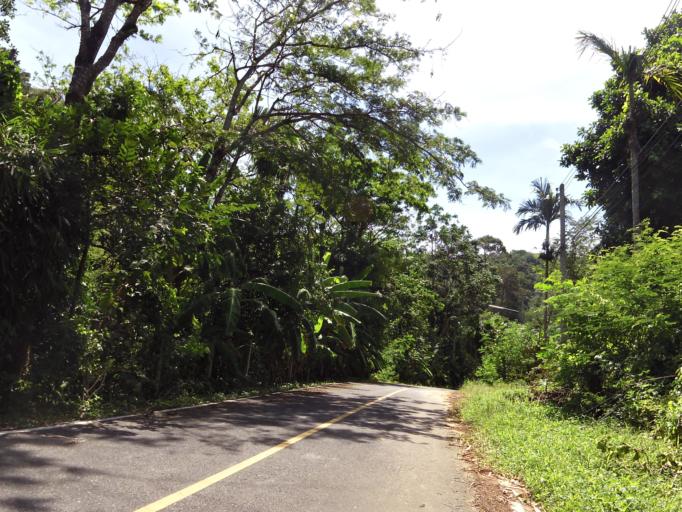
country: TH
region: Phuket
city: Ban Karon
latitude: 7.8469
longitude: 98.3082
